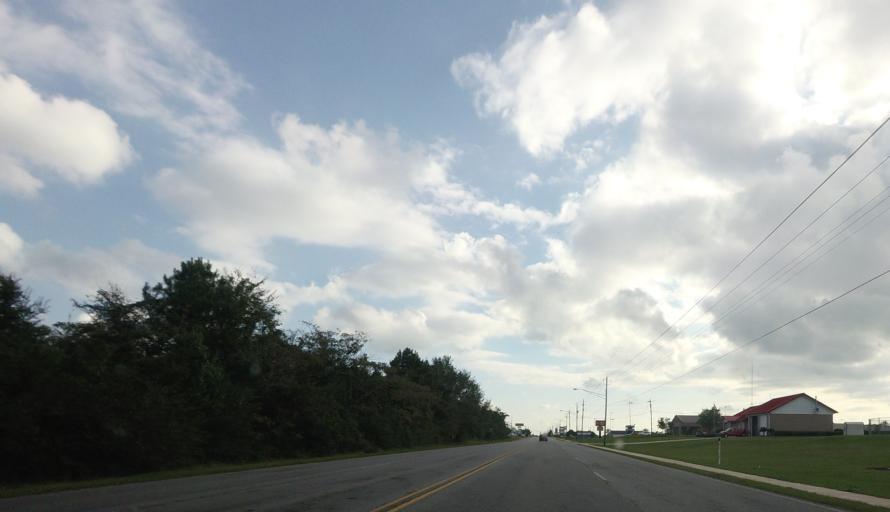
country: US
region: Georgia
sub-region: Houston County
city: Warner Robins
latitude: 32.6359
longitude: -83.6416
